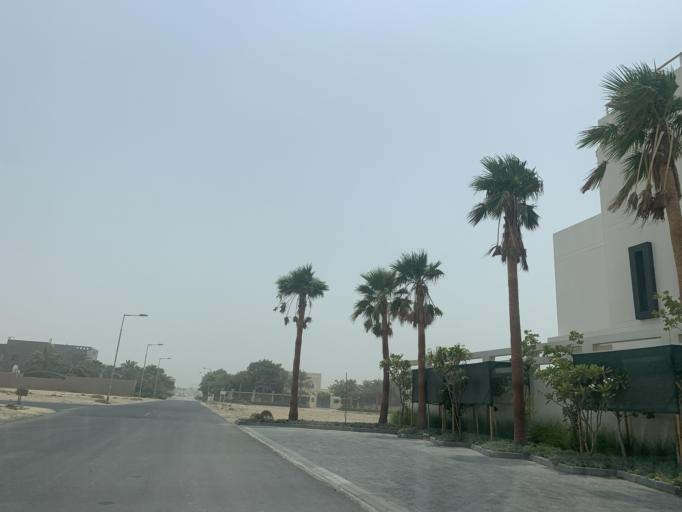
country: BH
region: Central Governorate
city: Madinat Hamad
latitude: 26.1700
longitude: 50.4763
